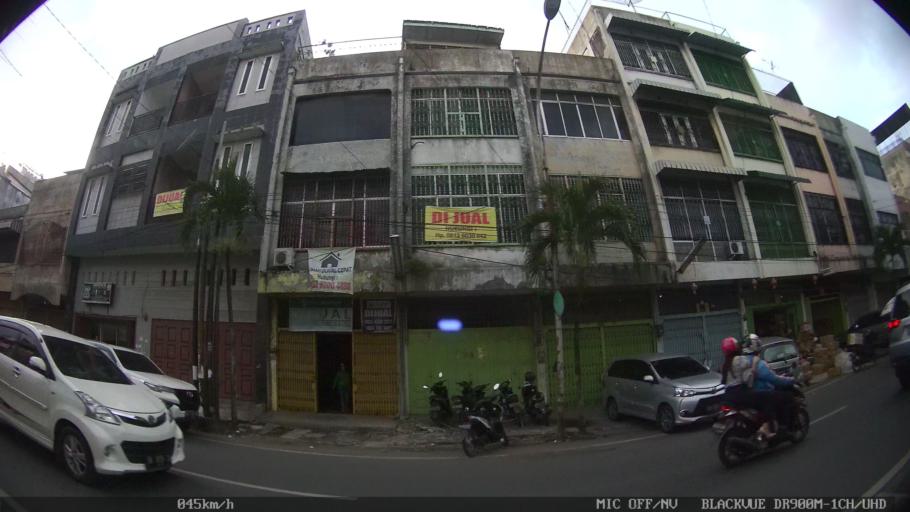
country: ID
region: North Sumatra
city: Medan
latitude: 3.5807
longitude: 98.6919
